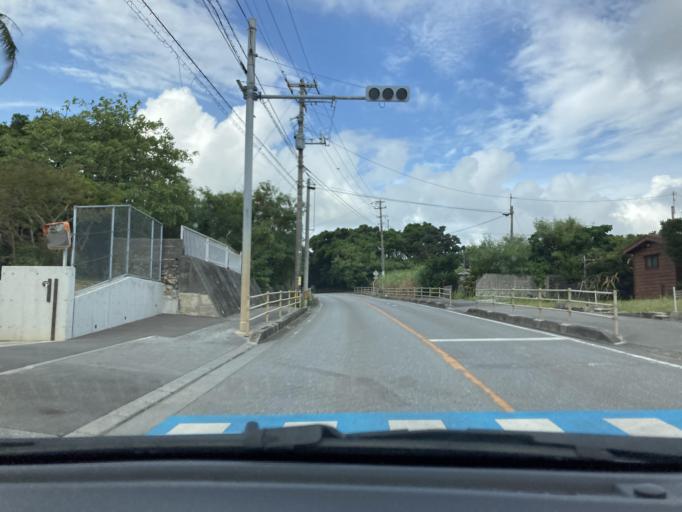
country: JP
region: Okinawa
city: Itoman
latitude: 26.0970
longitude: 127.6994
